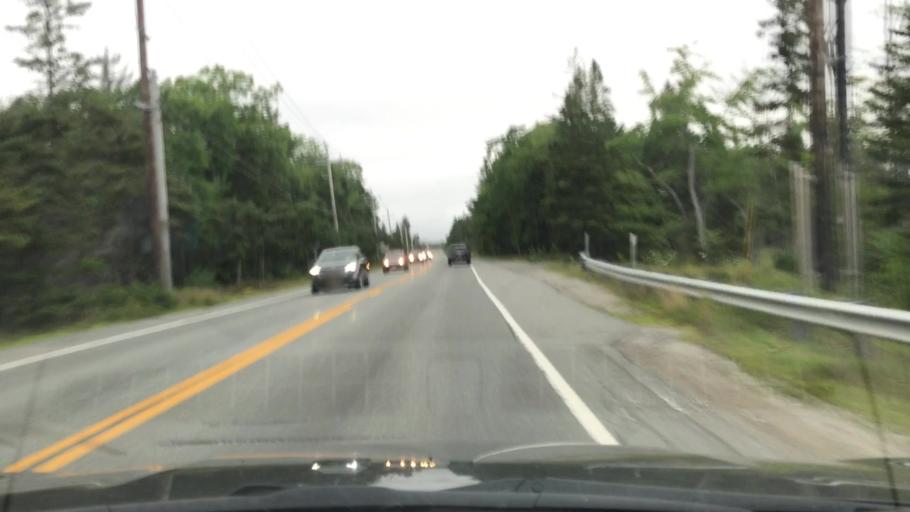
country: US
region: Maine
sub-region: Hancock County
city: Trenton
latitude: 44.4228
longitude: -68.3644
